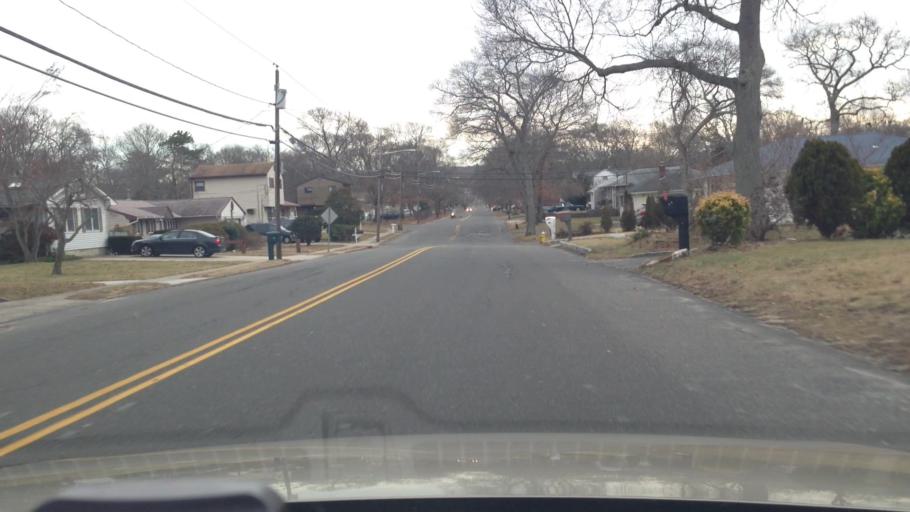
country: US
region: New York
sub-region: Suffolk County
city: Selden
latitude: 40.8599
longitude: -73.0344
